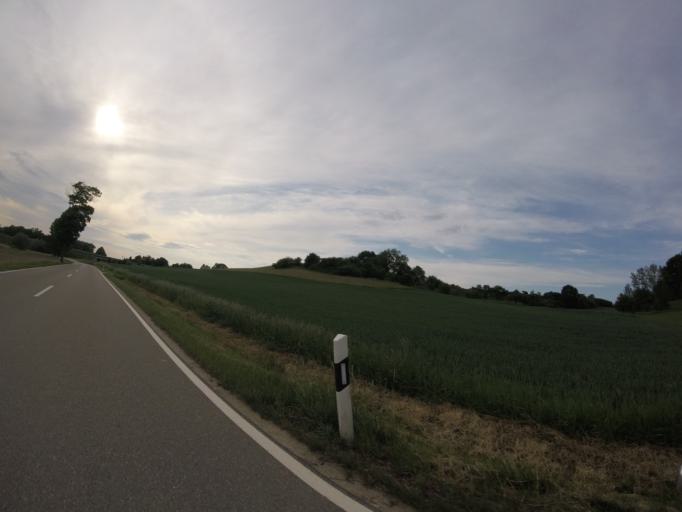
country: DE
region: Bavaria
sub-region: Upper Bavaria
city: Ilmmunster
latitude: 48.4836
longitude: 11.5133
